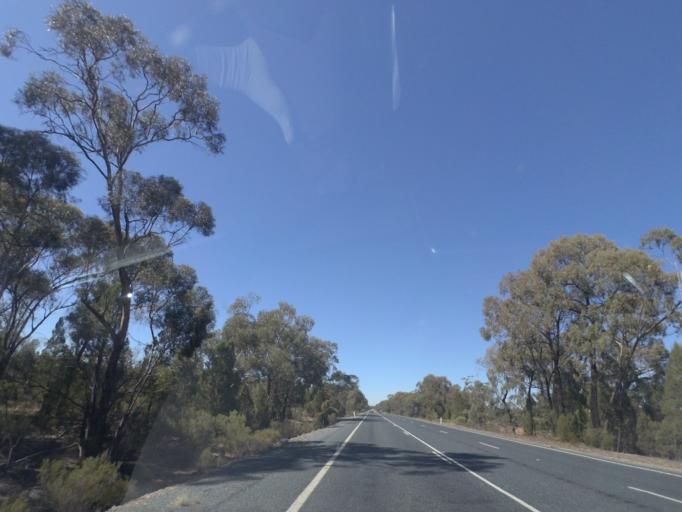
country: AU
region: New South Wales
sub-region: Bland
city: West Wyalong
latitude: -34.1296
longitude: 147.1241
